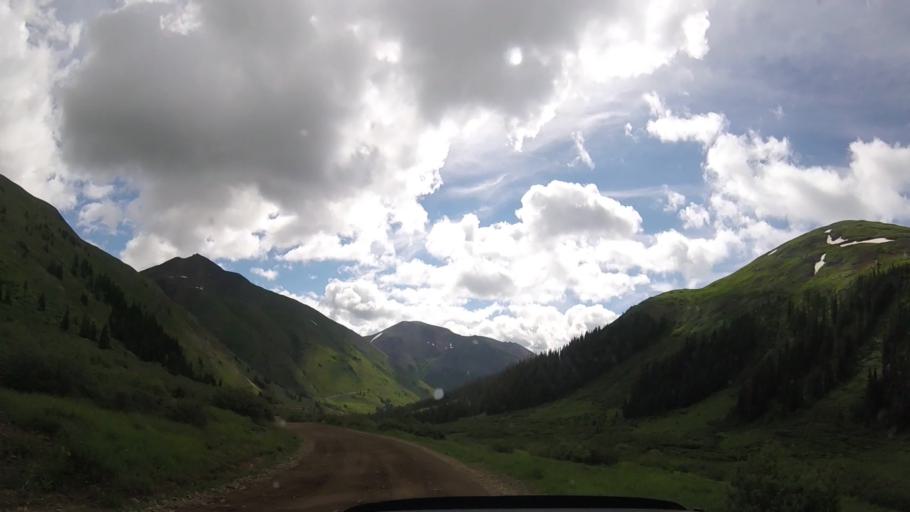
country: US
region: Colorado
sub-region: Ouray County
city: Ouray
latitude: 37.9317
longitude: -107.5857
